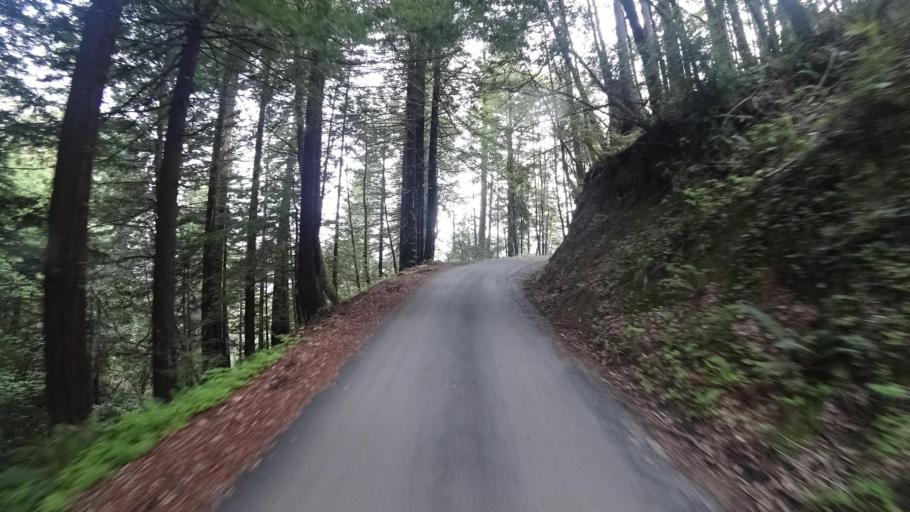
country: US
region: California
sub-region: Humboldt County
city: Redway
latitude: 40.3374
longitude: -123.9110
